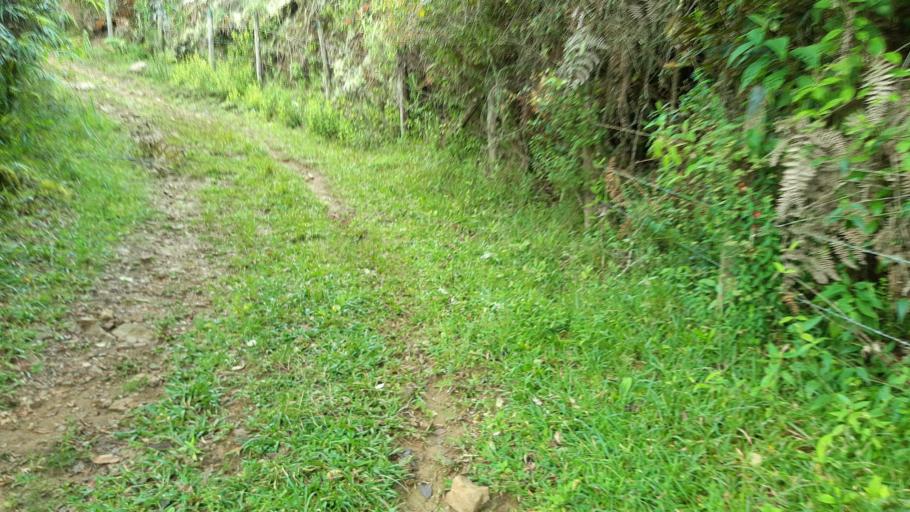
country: CO
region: Boyaca
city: Garagoa
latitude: 5.0862
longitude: -73.3181
